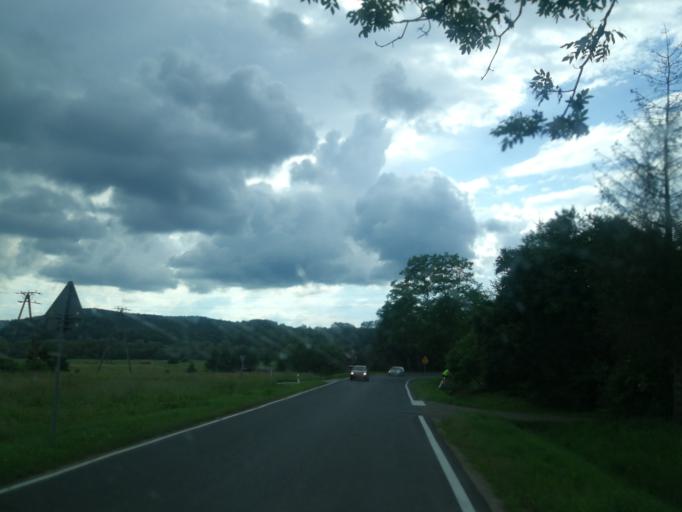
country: PL
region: Subcarpathian Voivodeship
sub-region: Powiat leski
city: Uherce Mineralne
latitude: 49.4600
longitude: 22.4045
